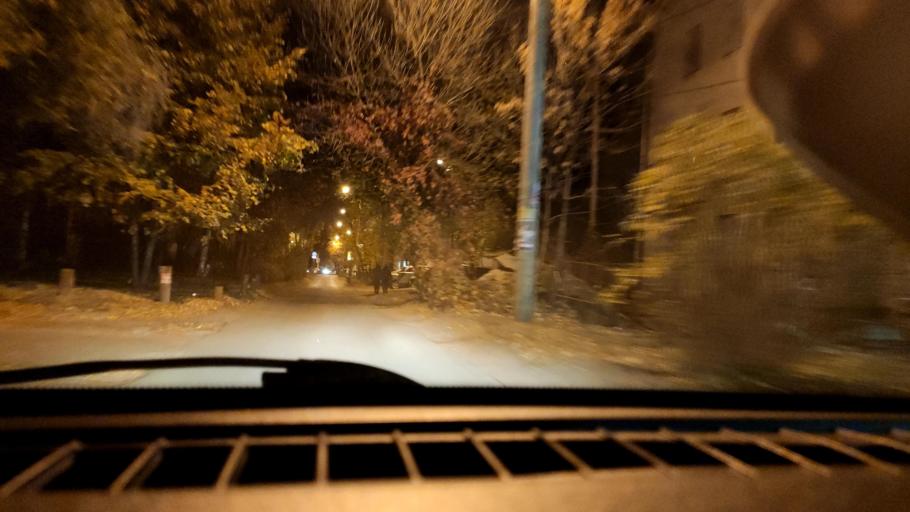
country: RU
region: Samara
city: Samara
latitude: 53.2016
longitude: 50.1830
